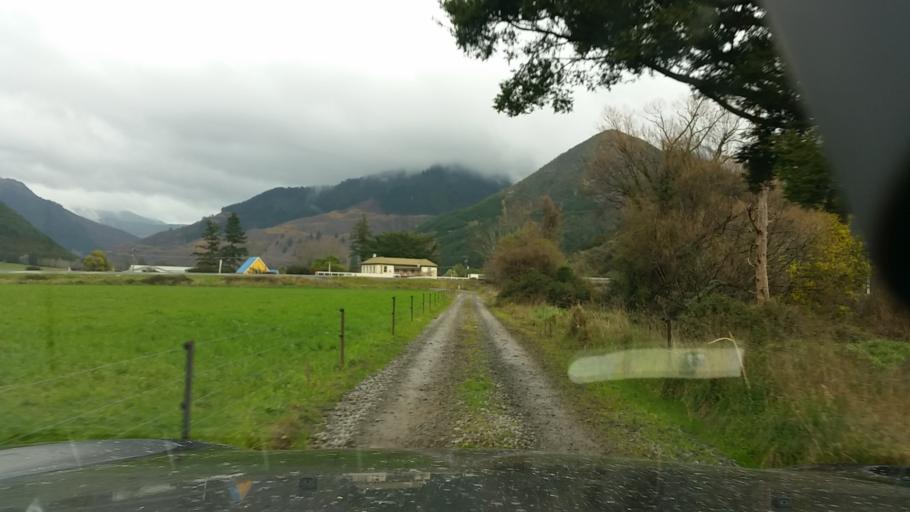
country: NZ
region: Marlborough
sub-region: Marlborough District
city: Picton
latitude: -41.2893
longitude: 173.6714
